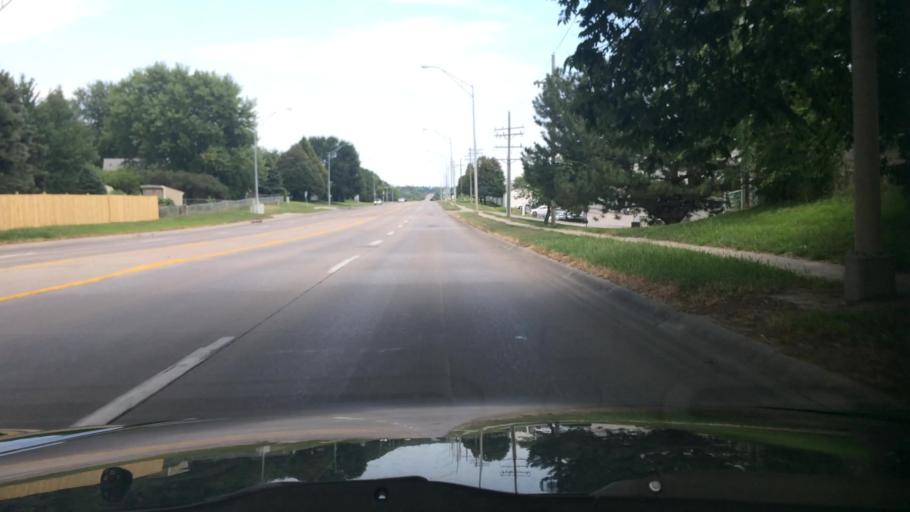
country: US
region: Nebraska
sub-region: Douglas County
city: Ralston
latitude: 41.2053
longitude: -96.0720
